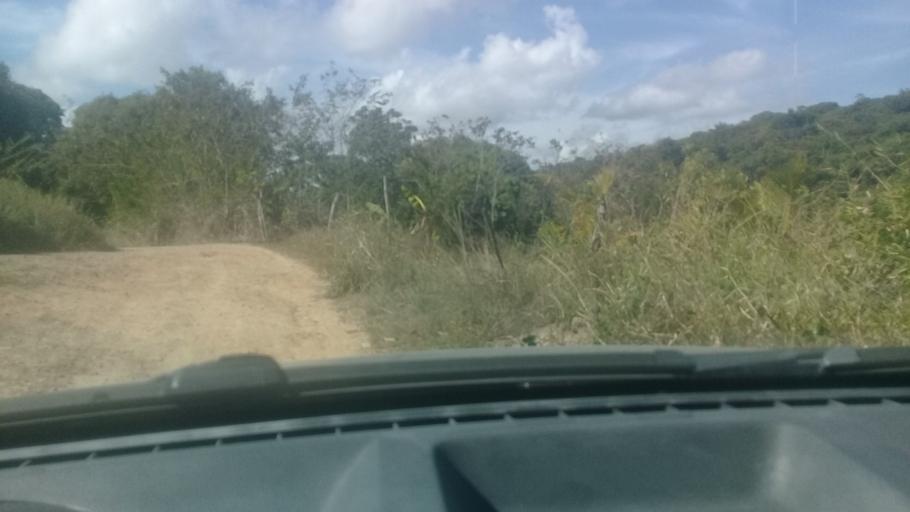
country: BR
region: Pernambuco
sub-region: Jaboatao Dos Guararapes
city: Jaboatao dos Guararapes
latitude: -8.0841
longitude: -35.0352
